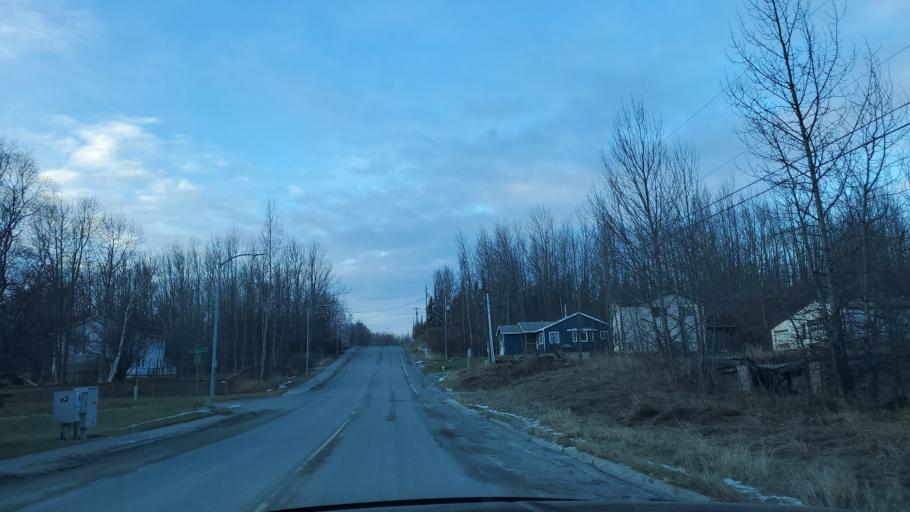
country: US
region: Alaska
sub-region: Matanuska-Susitna Borough
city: Palmer
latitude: 61.6139
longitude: -149.1098
